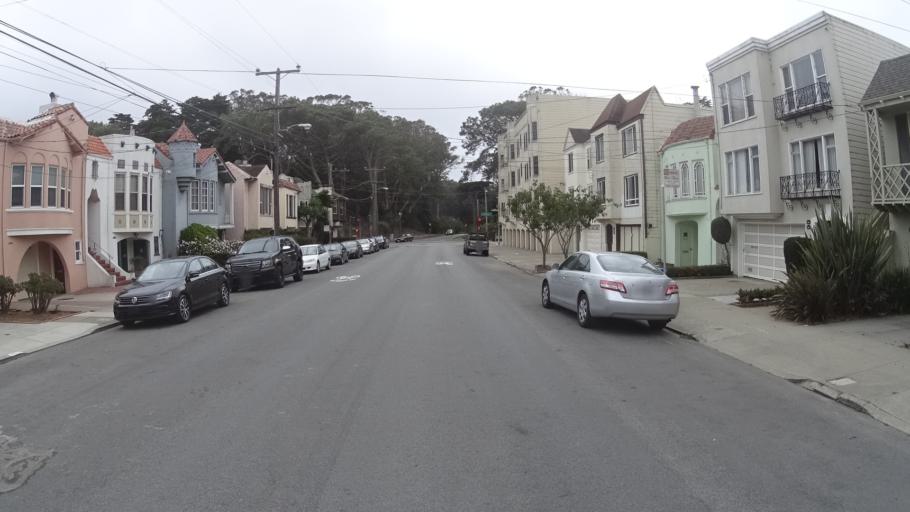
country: US
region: California
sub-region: San Francisco County
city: San Francisco
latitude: 37.7732
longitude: -122.4896
